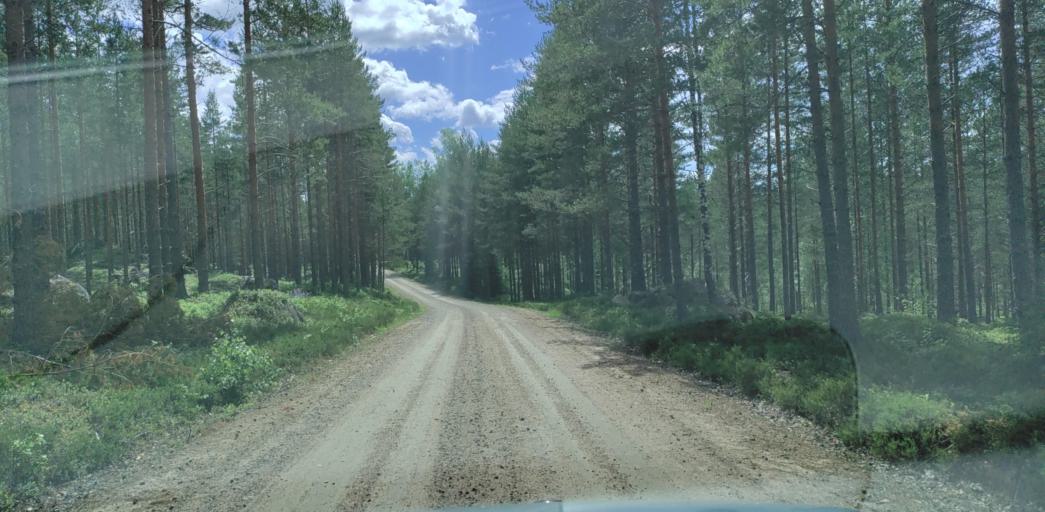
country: SE
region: Vaermland
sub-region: Hagfors Kommun
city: Ekshaerad
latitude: 60.0628
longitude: 13.2901
